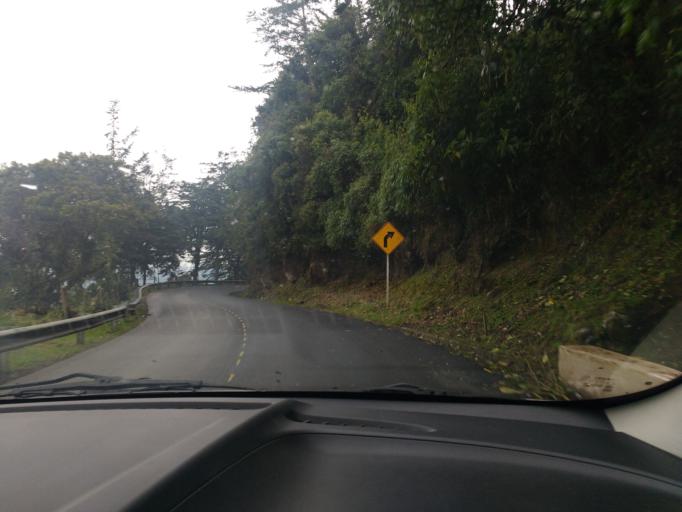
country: CO
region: Cundinamarca
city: Choachi
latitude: 4.5667
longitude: -73.9583
